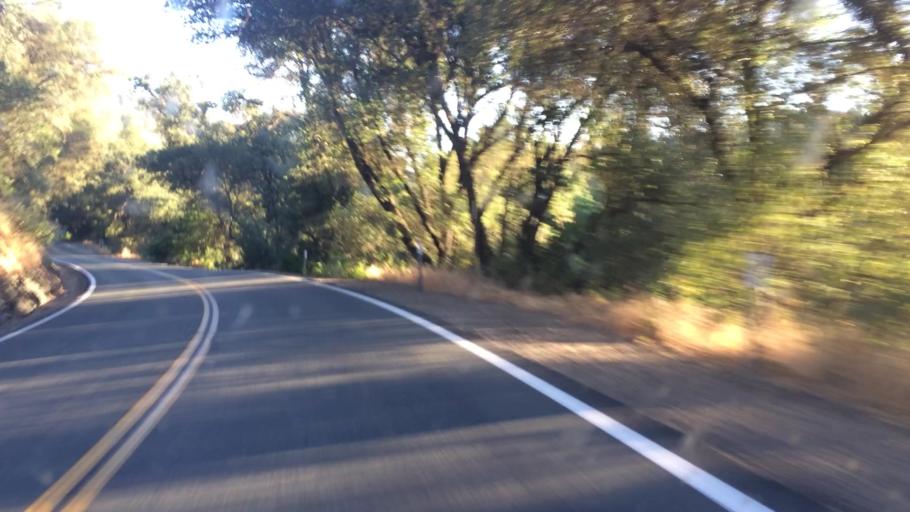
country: US
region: California
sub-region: Amador County
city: Plymouth
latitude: 38.5401
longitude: -120.8473
